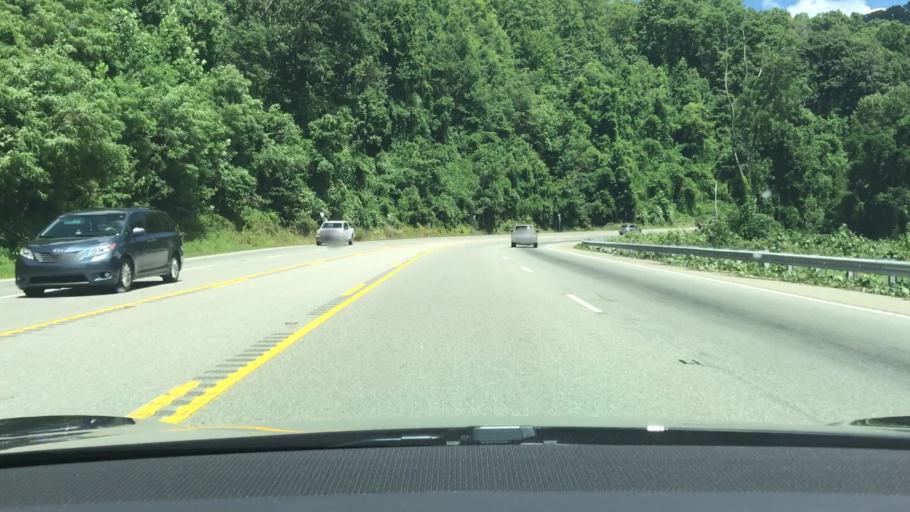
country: US
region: North Carolina
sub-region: Macon County
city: Franklin
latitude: 35.2538
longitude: -83.3169
